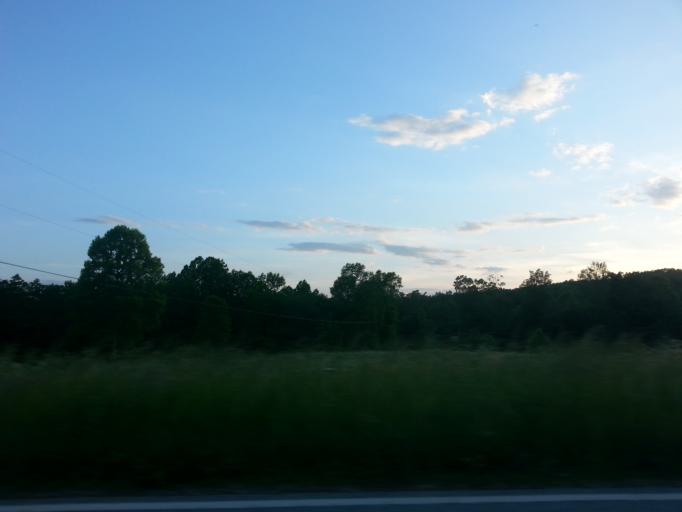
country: US
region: Tennessee
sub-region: Monroe County
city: Madisonville
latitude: 35.2966
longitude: -84.2898
